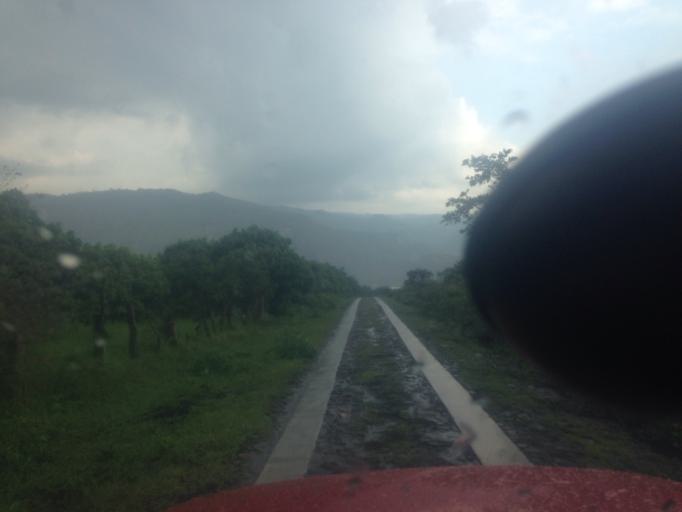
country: MX
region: Nayarit
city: Jala
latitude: 21.1153
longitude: -104.4674
